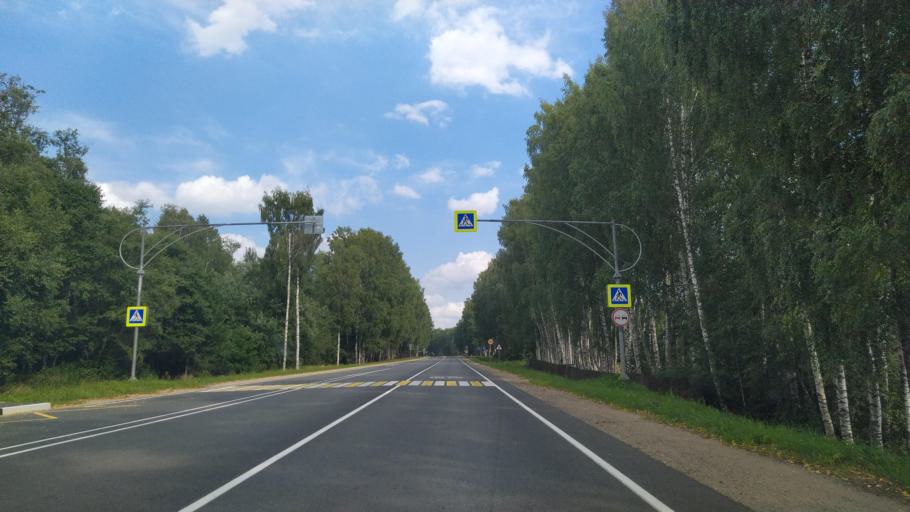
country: RU
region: Pskov
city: Dno
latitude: 57.9830
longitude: 29.7815
